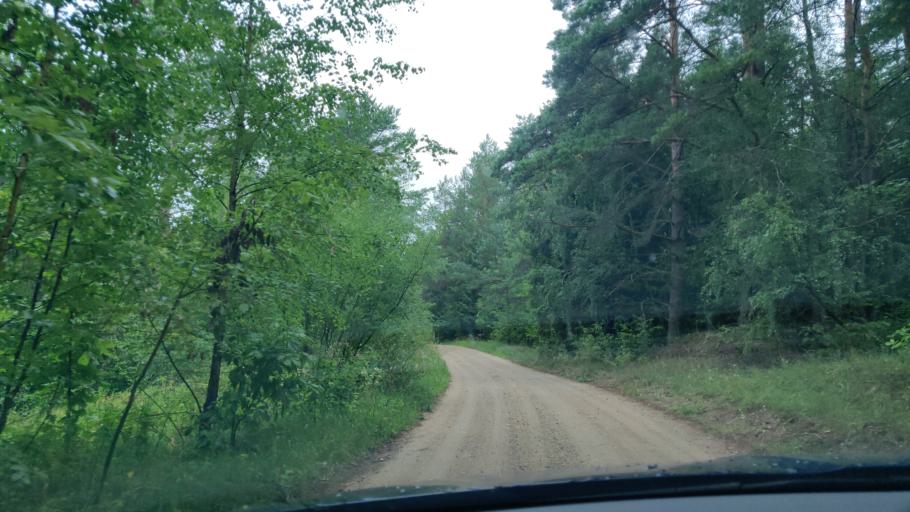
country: LT
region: Vilnius County
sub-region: Trakai
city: Rudiskes
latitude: 54.6070
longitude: 24.8434
